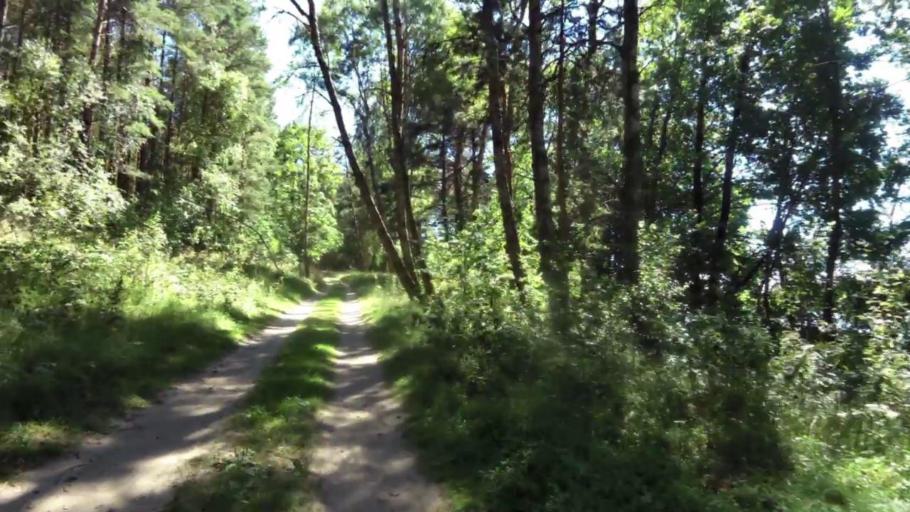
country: PL
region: West Pomeranian Voivodeship
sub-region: Powiat szczecinecki
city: Bialy Bor
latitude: 53.8496
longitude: 16.8704
